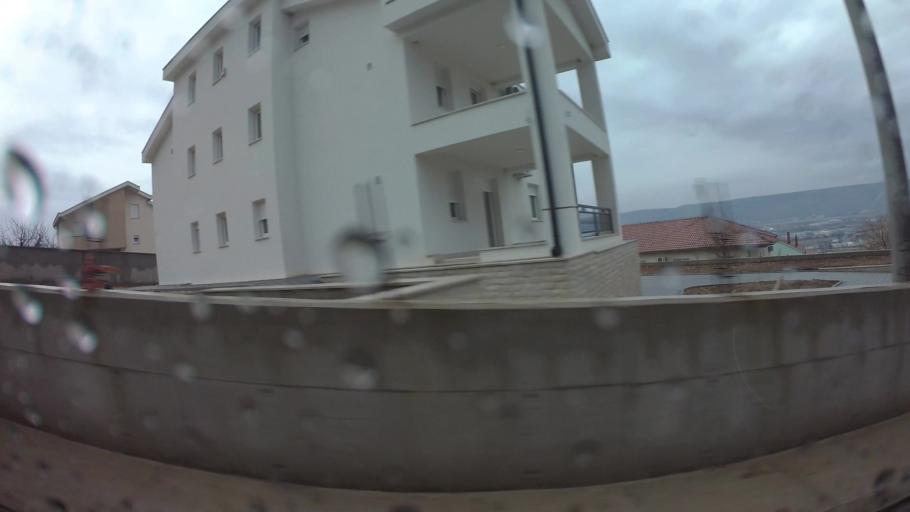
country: BA
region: Federation of Bosnia and Herzegovina
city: Rodoc
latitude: 43.3059
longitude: 17.8481
